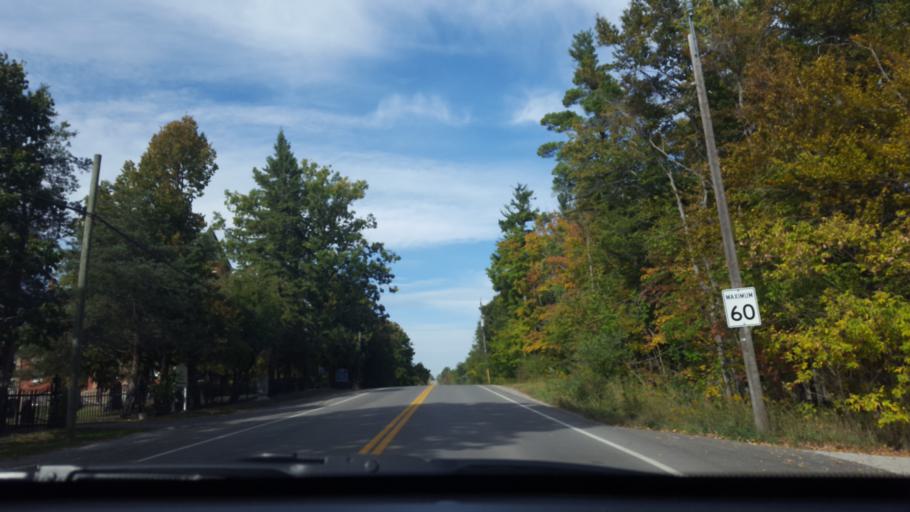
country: CA
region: Ontario
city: Vaughan
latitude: 43.8425
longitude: -79.5870
